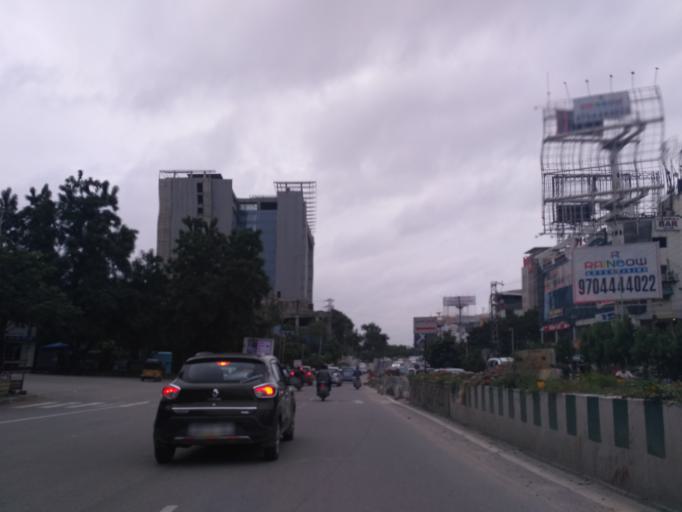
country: IN
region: Telangana
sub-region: Rangareddi
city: Kukatpalli
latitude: 17.4466
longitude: 78.3776
